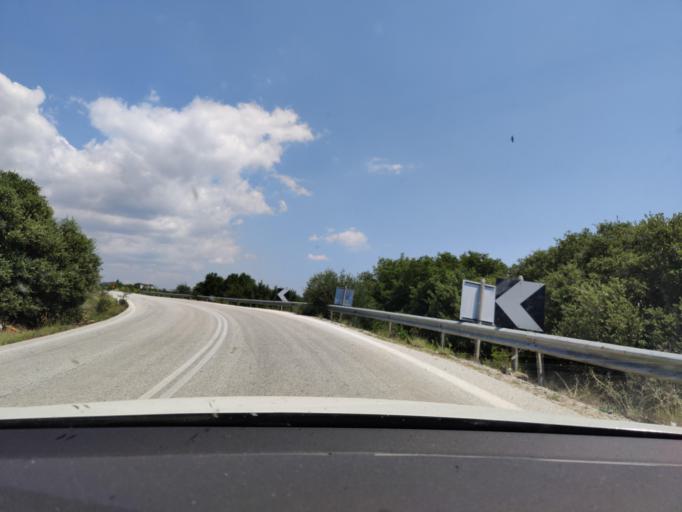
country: GR
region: East Macedonia and Thrace
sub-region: Nomos Kavalas
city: Paralia Ofryniou
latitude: 40.8076
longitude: 23.9804
